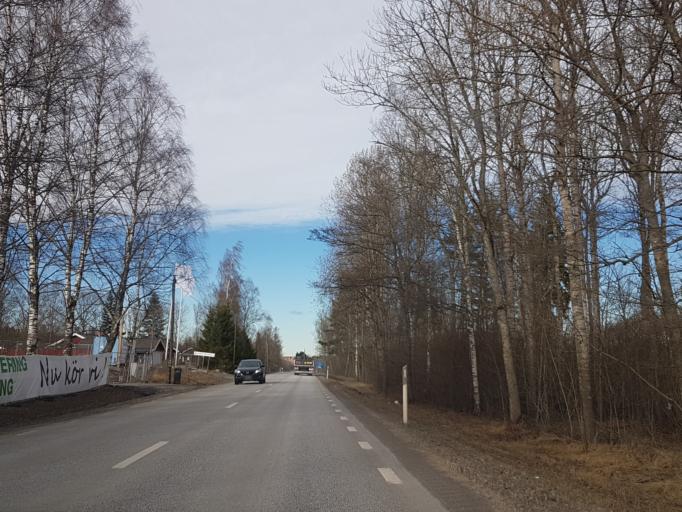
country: SE
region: Stockholm
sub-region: Norrtalje Kommun
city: Norrtalje
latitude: 59.7351
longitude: 18.6850
